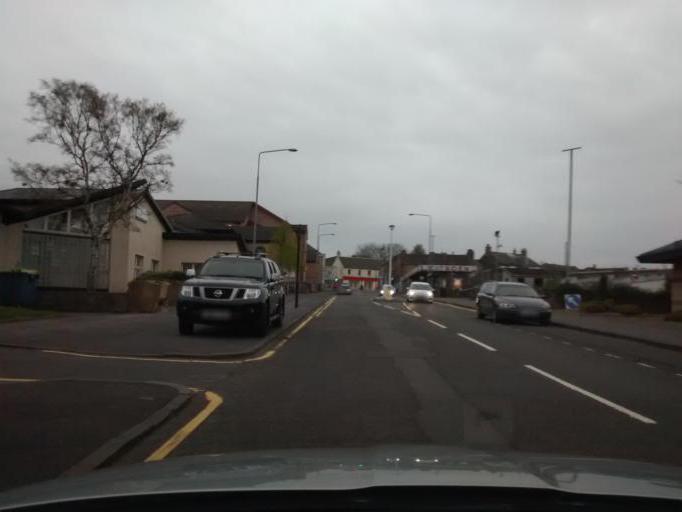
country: GB
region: Scotland
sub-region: West Lothian
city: Armadale
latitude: 55.9001
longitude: -3.6990
